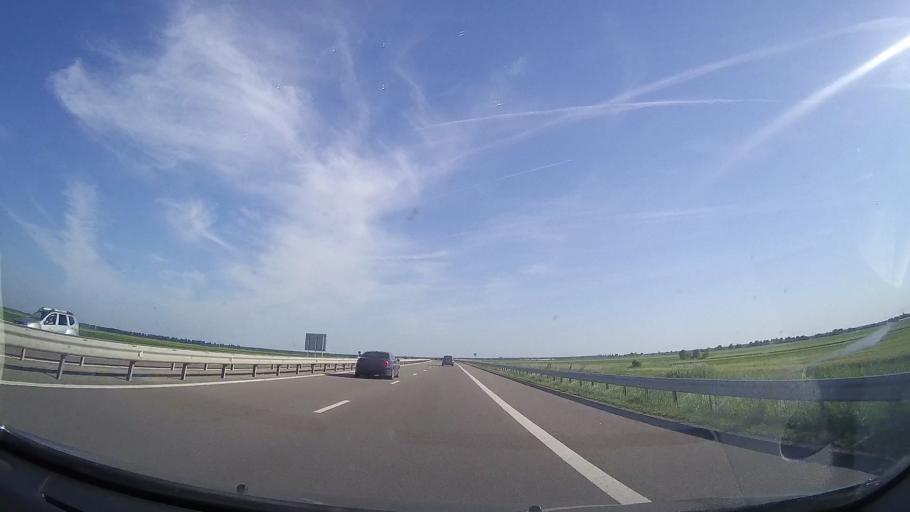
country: RO
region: Ilfov
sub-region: Comuna Gruiu
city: Gruiu
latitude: 44.7471
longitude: 26.2561
